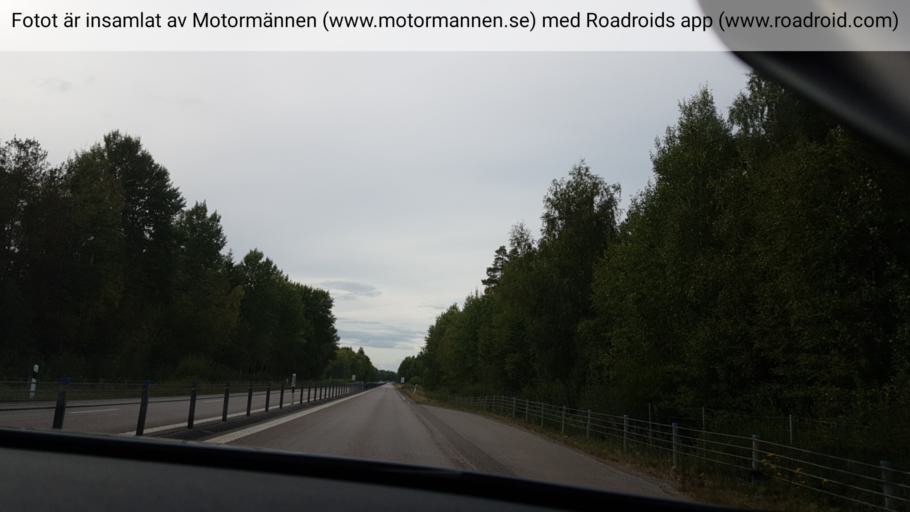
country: SE
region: Vaestra Goetaland
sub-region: Skovde Kommun
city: Stopen
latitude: 58.5171
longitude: 13.8319
